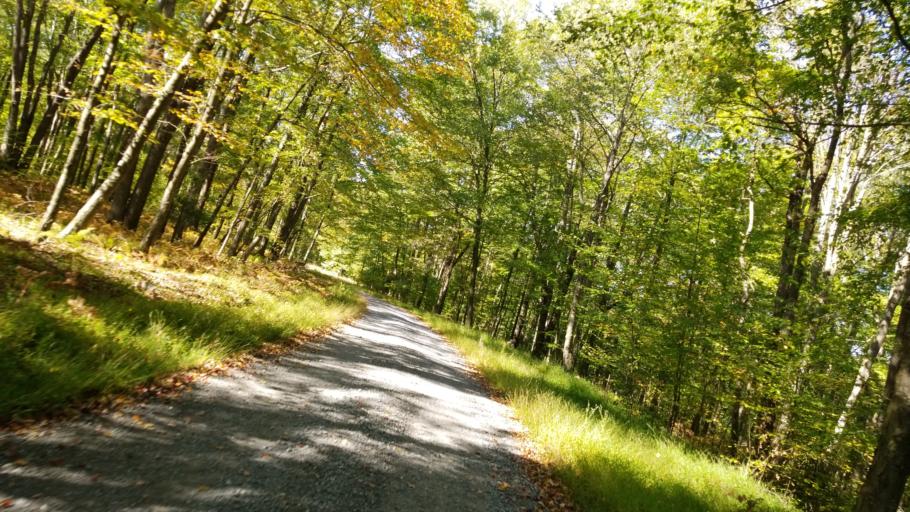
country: US
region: Pennsylvania
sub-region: Clearfield County
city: Clearfield
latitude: 41.1830
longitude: -78.4993
